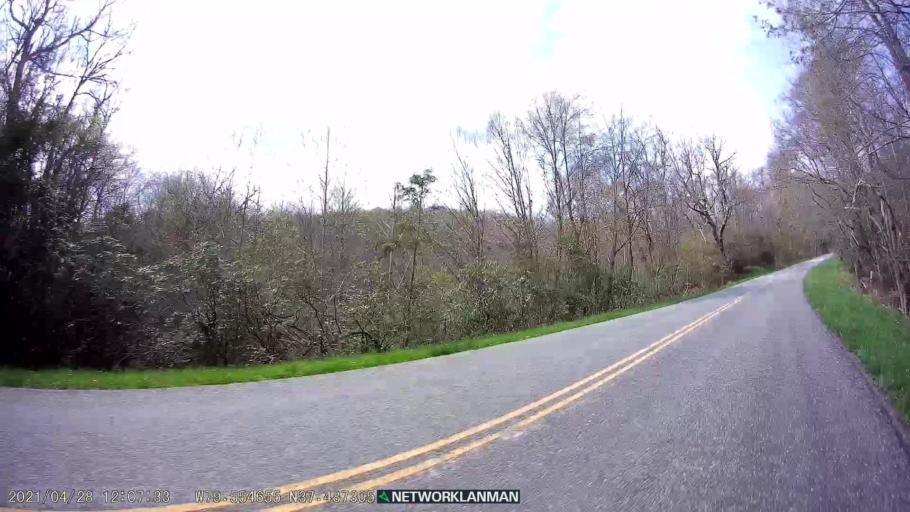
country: US
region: Virginia
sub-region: Botetourt County
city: Buchanan
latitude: 37.4875
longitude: -79.5548
